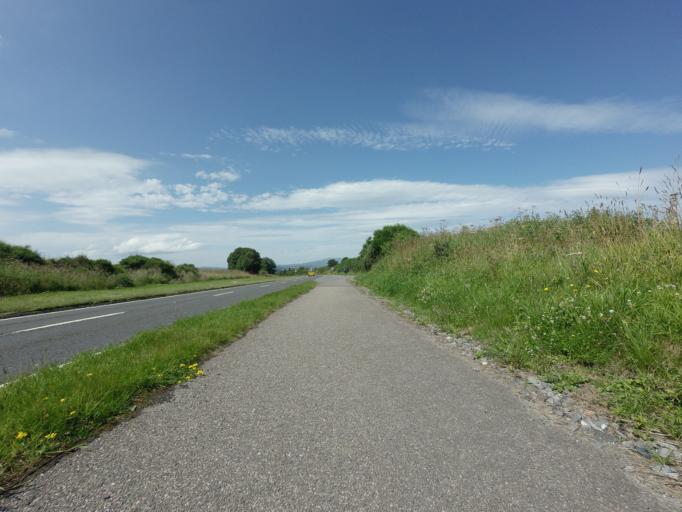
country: GB
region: Scotland
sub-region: Highland
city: Conon Bridge
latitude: 57.5488
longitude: -4.3925
